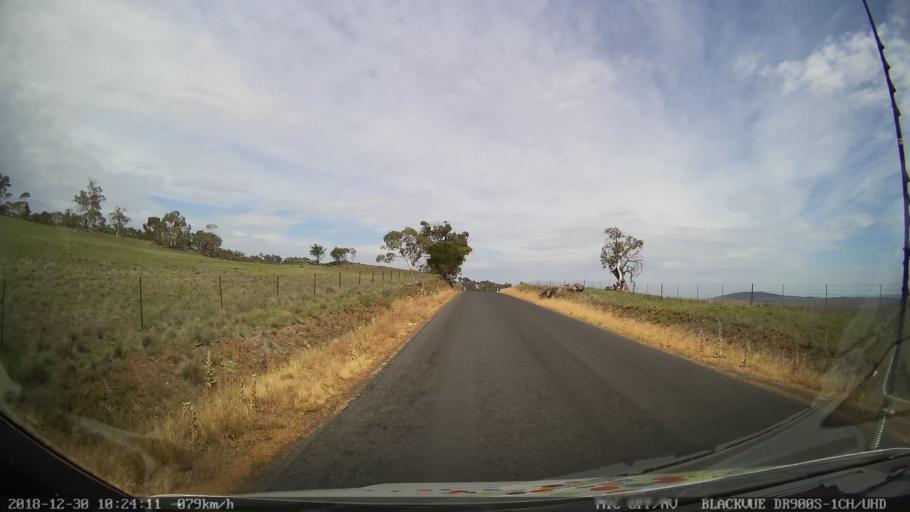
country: AU
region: New South Wales
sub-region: Snowy River
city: Berridale
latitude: -36.5322
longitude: 148.9728
